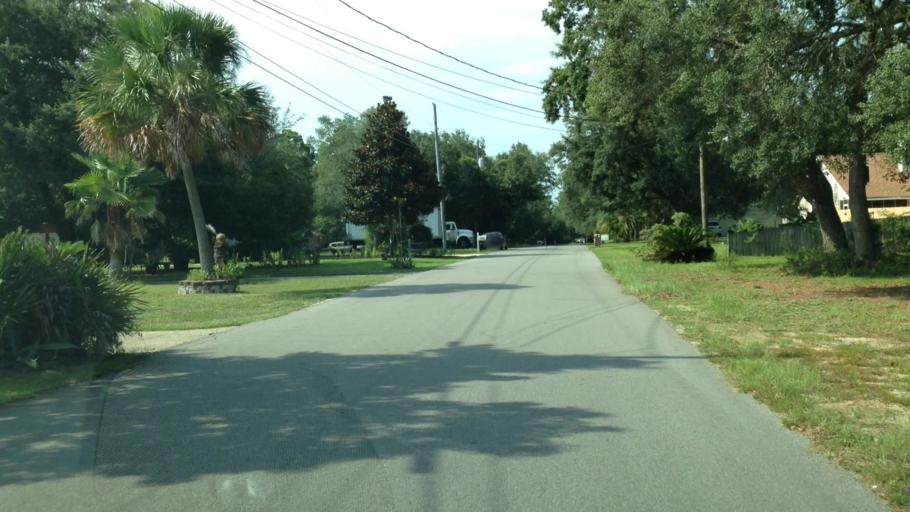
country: US
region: Florida
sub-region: Santa Rosa County
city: Holley
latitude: 30.4334
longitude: -86.9354
